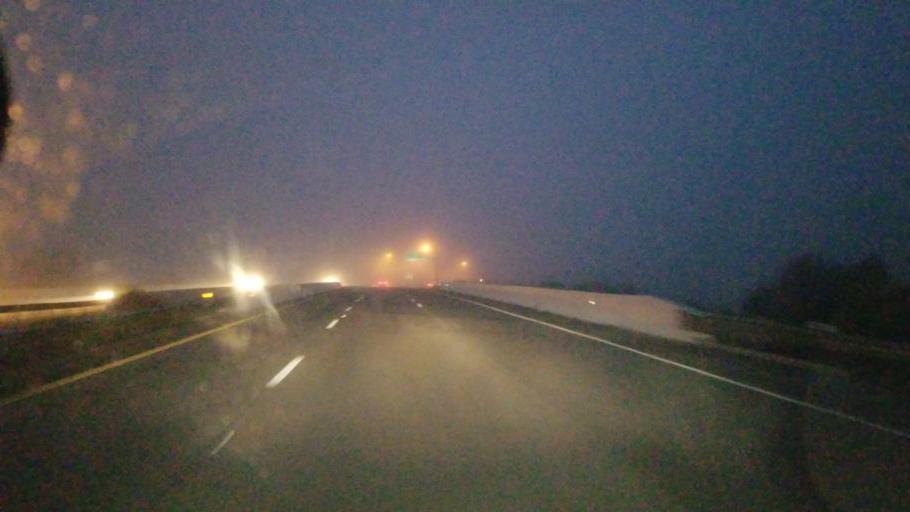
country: US
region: Ohio
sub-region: Ross County
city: Chillicothe
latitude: 39.3191
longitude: -82.9398
